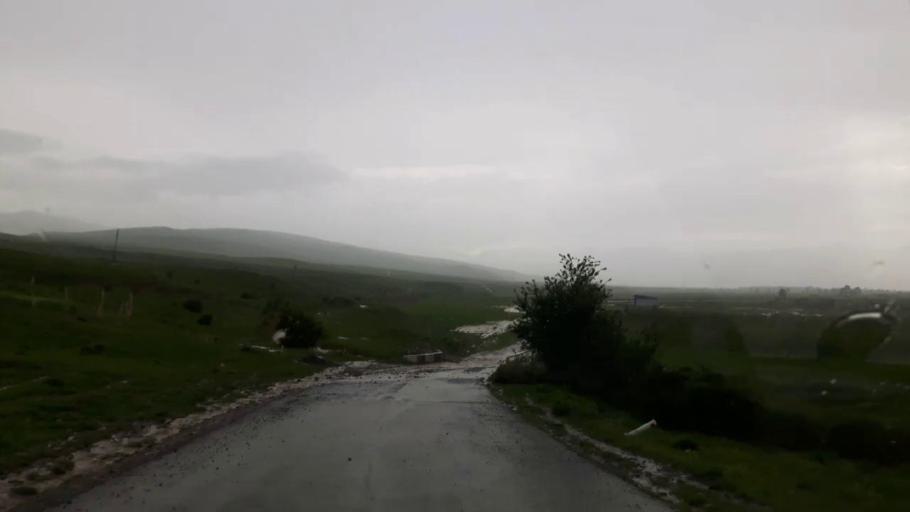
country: GE
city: Agara
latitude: 42.0143
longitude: 43.8256
